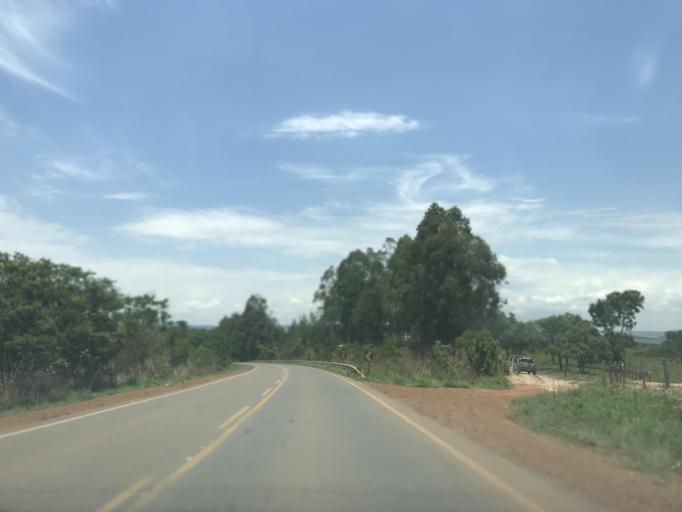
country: BR
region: Goias
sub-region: Vianopolis
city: Vianopolis
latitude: -16.5986
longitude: -48.3486
